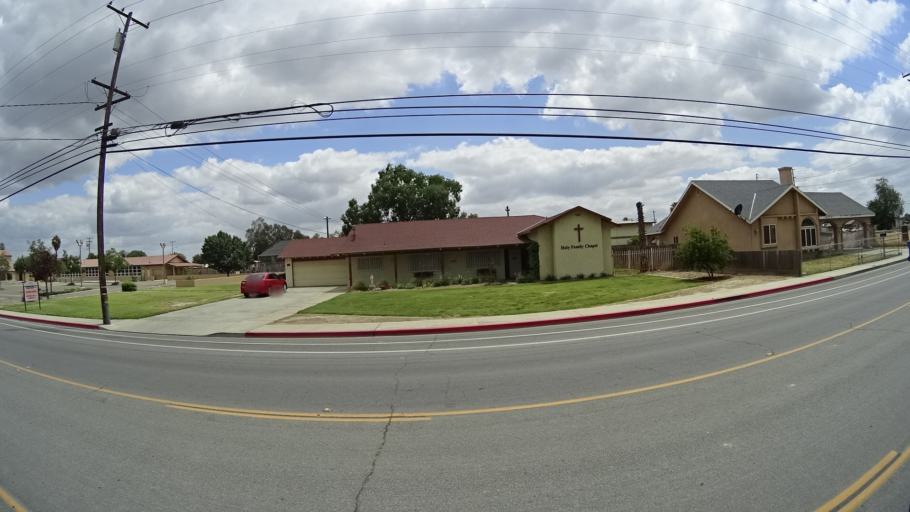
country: US
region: California
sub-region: Kings County
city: Home Garden
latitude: 36.3135
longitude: -119.6448
